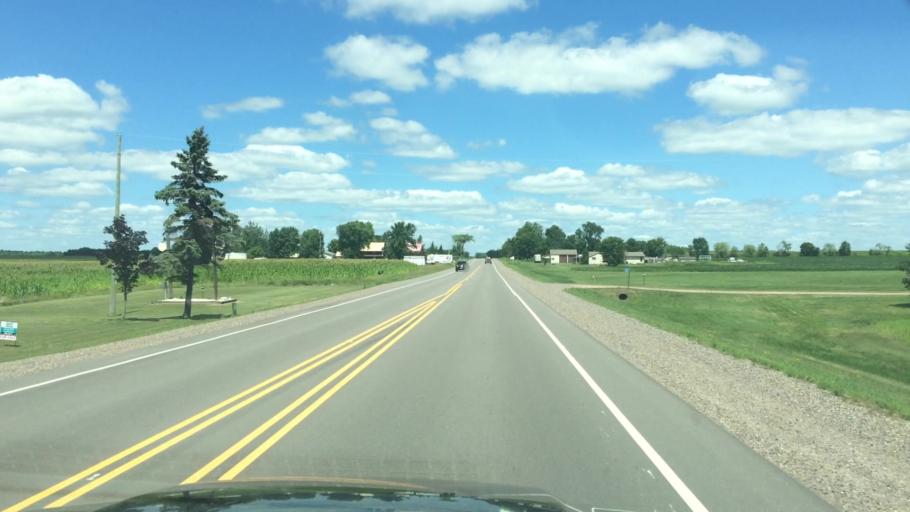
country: US
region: Wisconsin
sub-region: Clark County
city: Abbotsford
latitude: 45.0067
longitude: -90.3156
